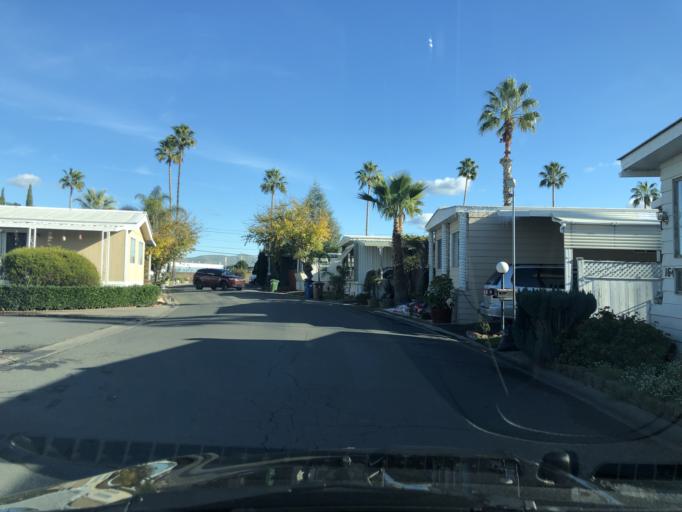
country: US
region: California
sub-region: Contra Costa County
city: Pacheco
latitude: 37.9871
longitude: -122.0641
